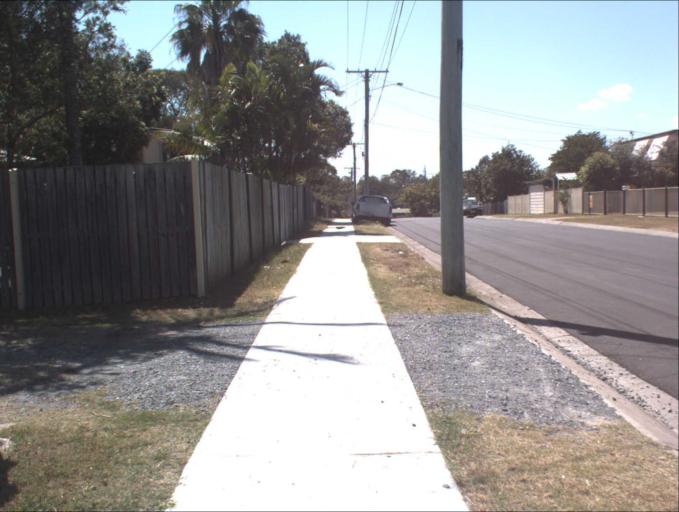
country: AU
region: Queensland
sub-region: Logan
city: Beenleigh
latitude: -27.7026
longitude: 153.2074
